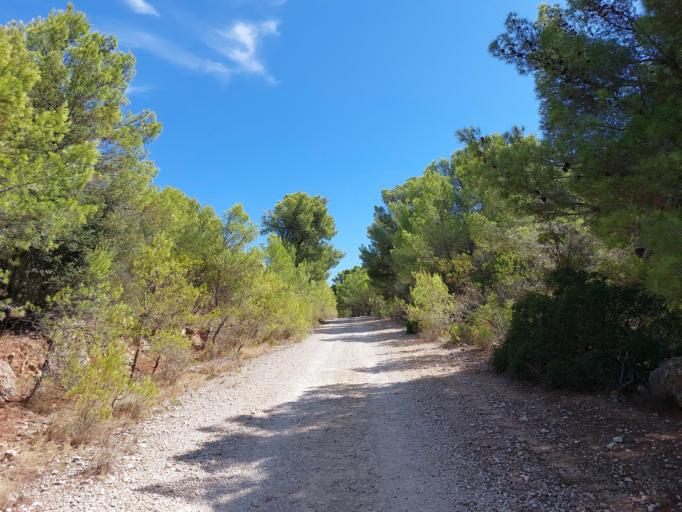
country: HR
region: Dubrovacko-Neretvanska
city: Smokvica
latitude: 42.7367
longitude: 16.8321
